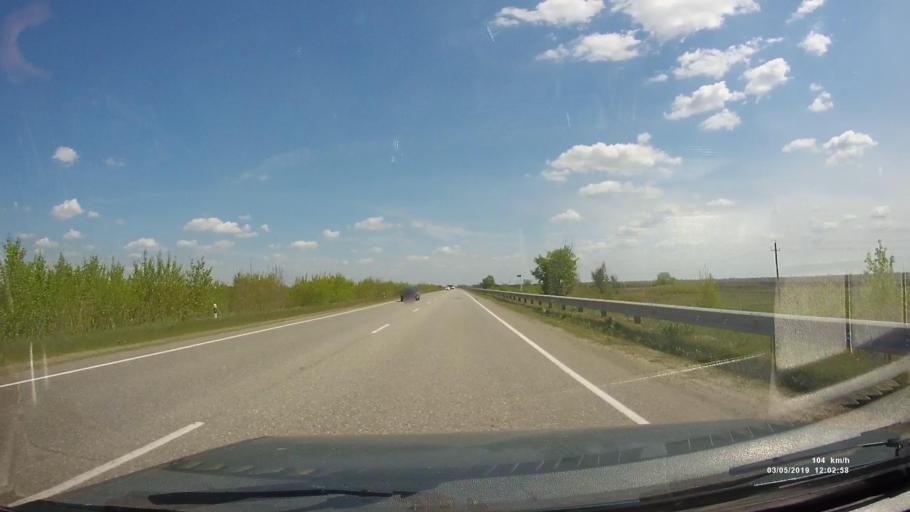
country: RU
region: Rostov
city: Bagayevskaya
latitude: 47.2729
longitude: 40.3798
